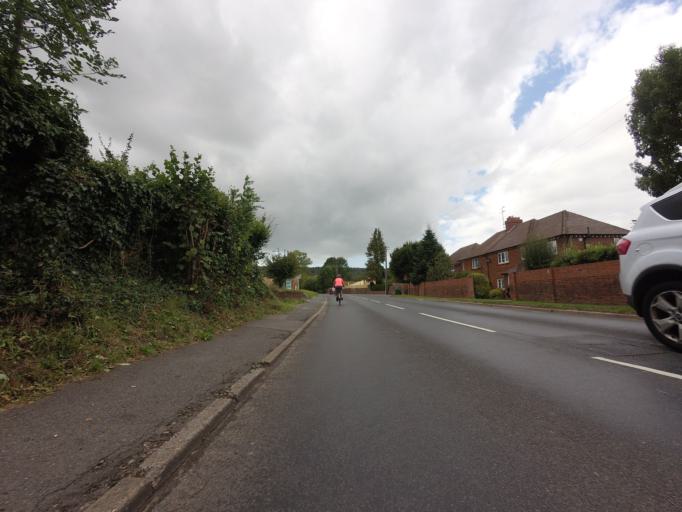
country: GB
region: England
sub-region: Kent
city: Shoreham
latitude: 51.3120
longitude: 0.1747
